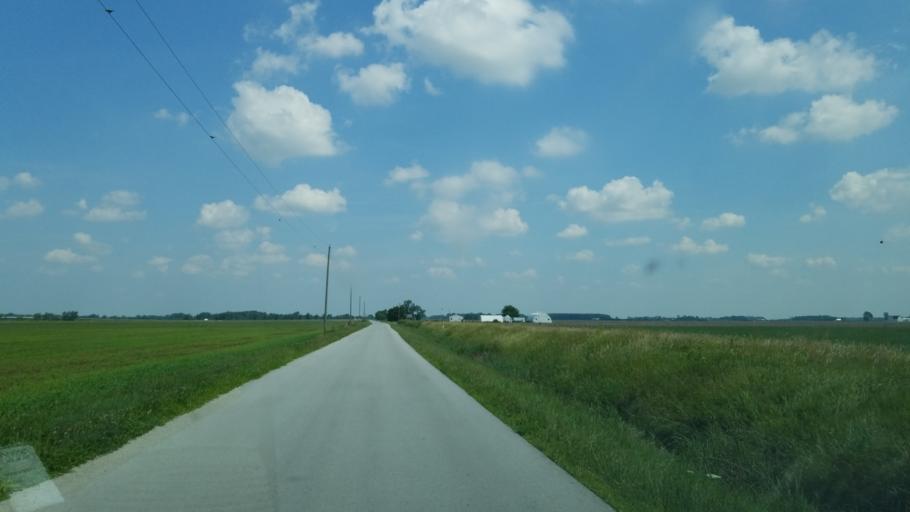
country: US
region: Ohio
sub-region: Wood County
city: North Baltimore
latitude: 41.2702
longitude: -83.6312
